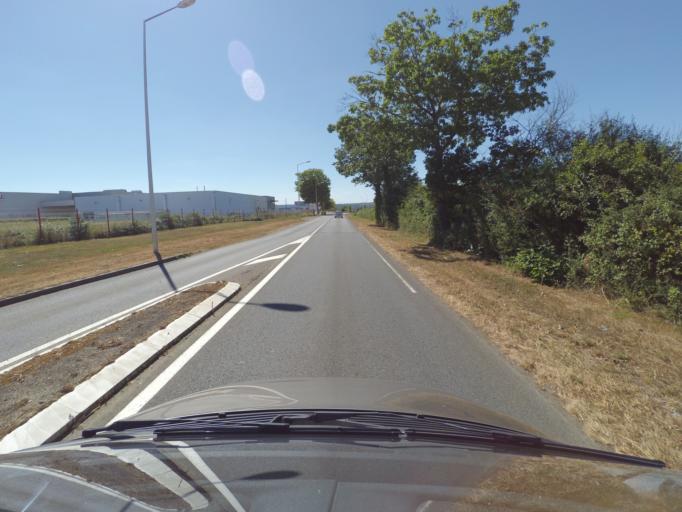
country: FR
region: Pays de la Loire
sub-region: Departement de Maine-et-Loire
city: Vihiers
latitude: 47.1477
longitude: -0.5194
